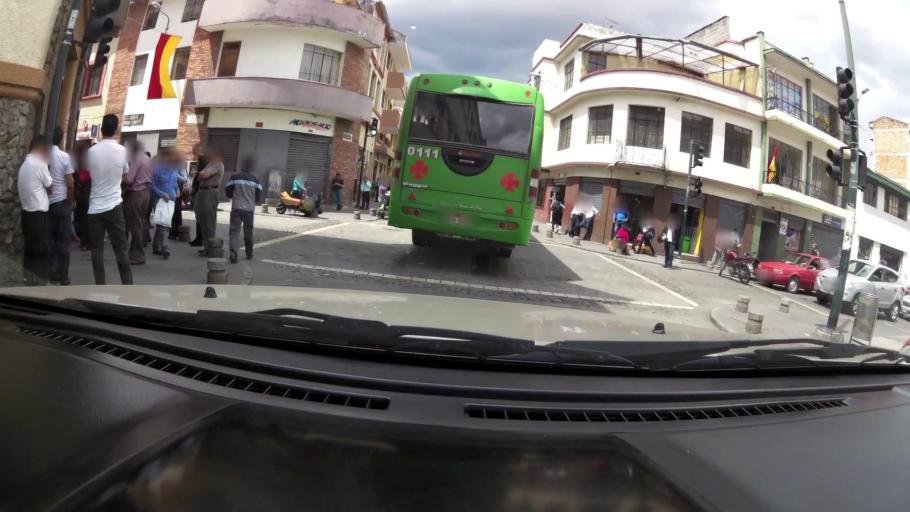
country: EC
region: Azuay
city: Cuenca
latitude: -2.8982
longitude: -79.0000
